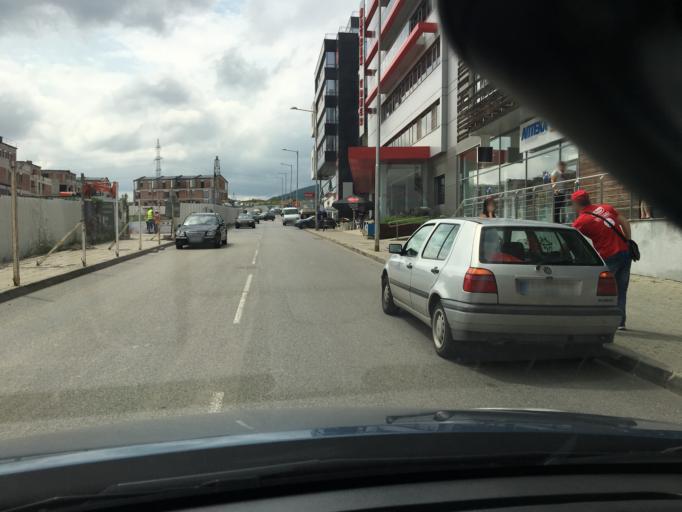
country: BG
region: Sofia-Capital
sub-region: Stolichna Obshtina
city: Sofia
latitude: 42.6225
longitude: 23.3699
